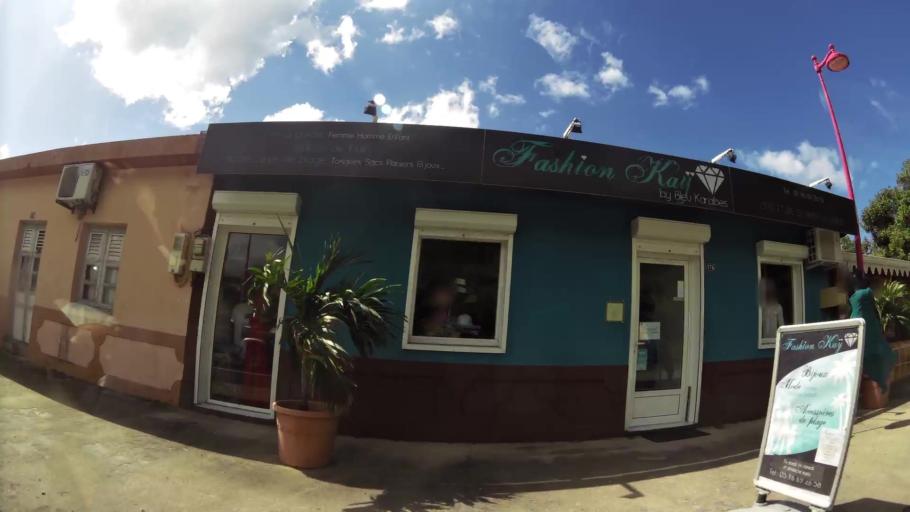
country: MQ
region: Martinique
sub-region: Martinique
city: Saint-Pierre
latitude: 14.6993
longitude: -61.1804
